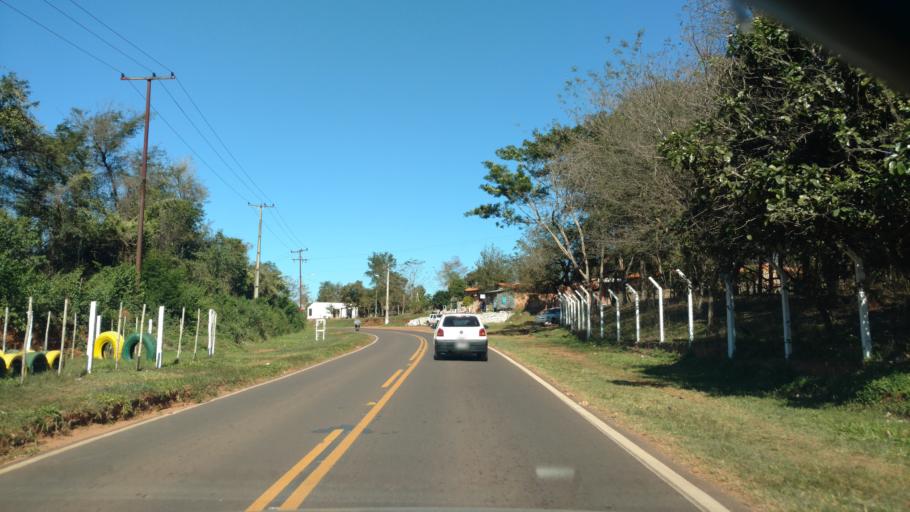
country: PY
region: Paraguari
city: Yaguaron
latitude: -25.5515
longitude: -57.2827
